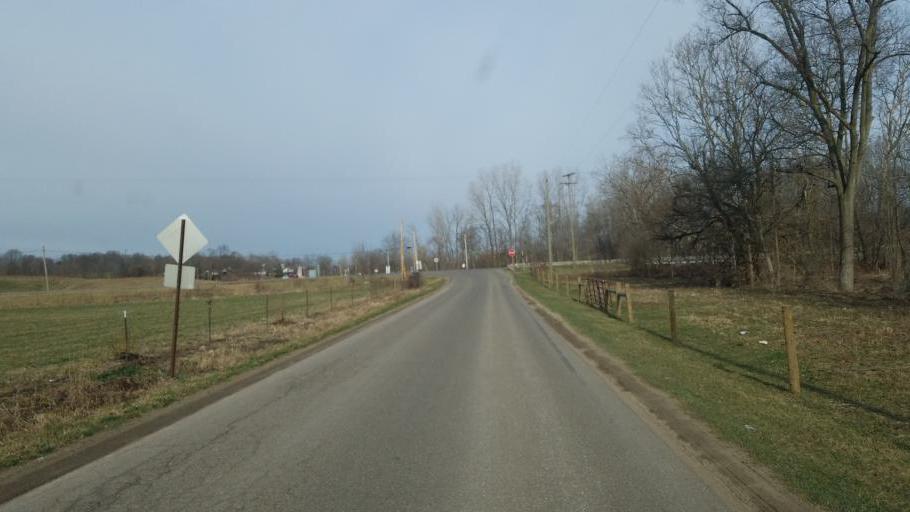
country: US
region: Ohio
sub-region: Knox County
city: Fredericktown
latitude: 40.5496
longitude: -82.6607
